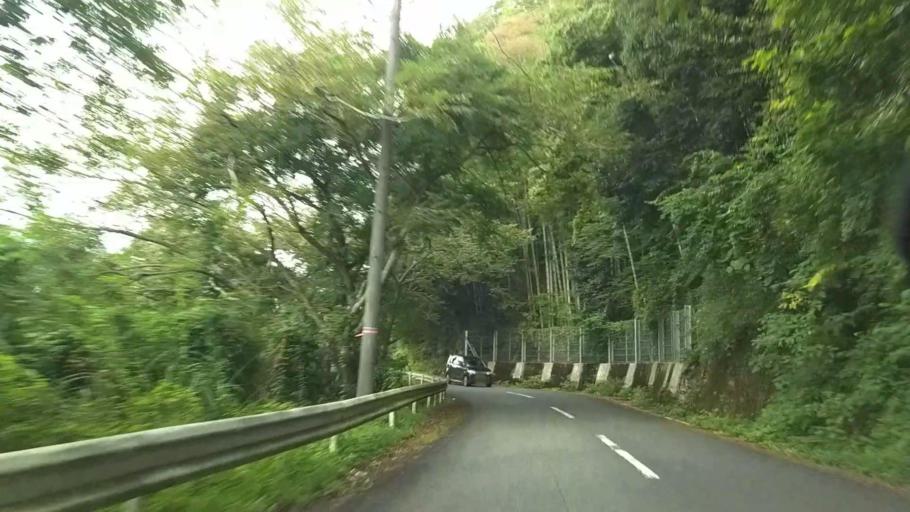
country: JP
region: Shizuoka
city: Fujinomiya
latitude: 35.2058
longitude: 138.5473
